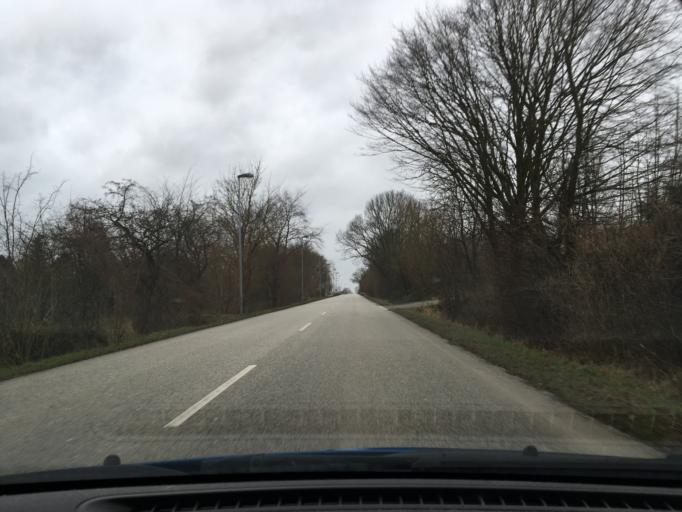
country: DE
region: Schleswig-Holstein
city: Lauenburg
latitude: 53.3817
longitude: 10.5454
